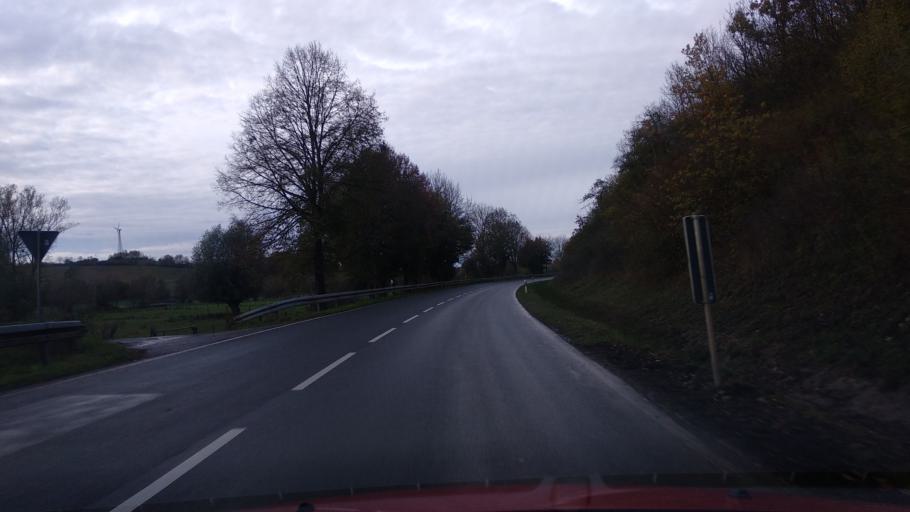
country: DE
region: North Rhine-Westphalia
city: Brakel
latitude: 51.6942
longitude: 9.2181
